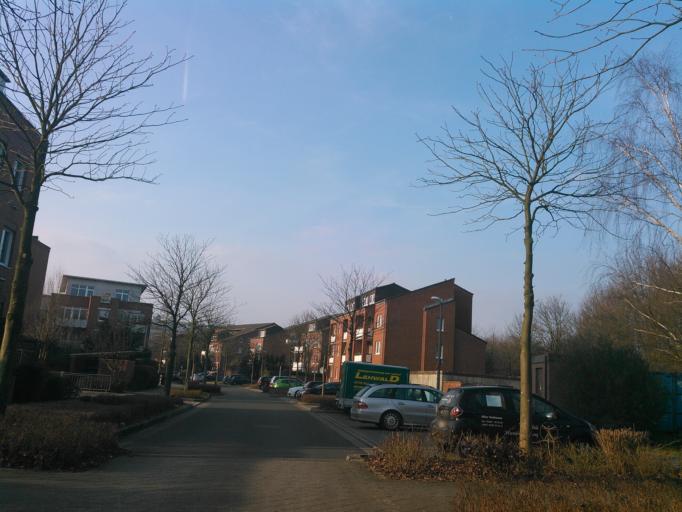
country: DE
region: North Rhine-Westphalia
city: Marl
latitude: 51.6535
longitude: 7.1031
